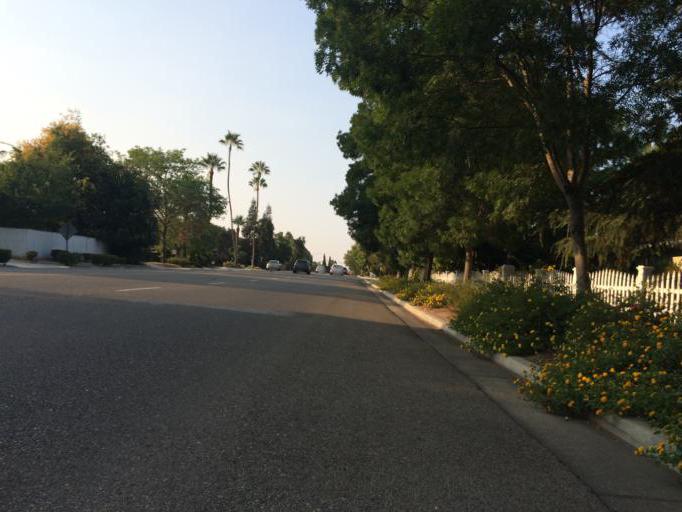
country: US
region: California
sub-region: Fresno County
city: Fresno
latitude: 36.8166
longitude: -119.8173
